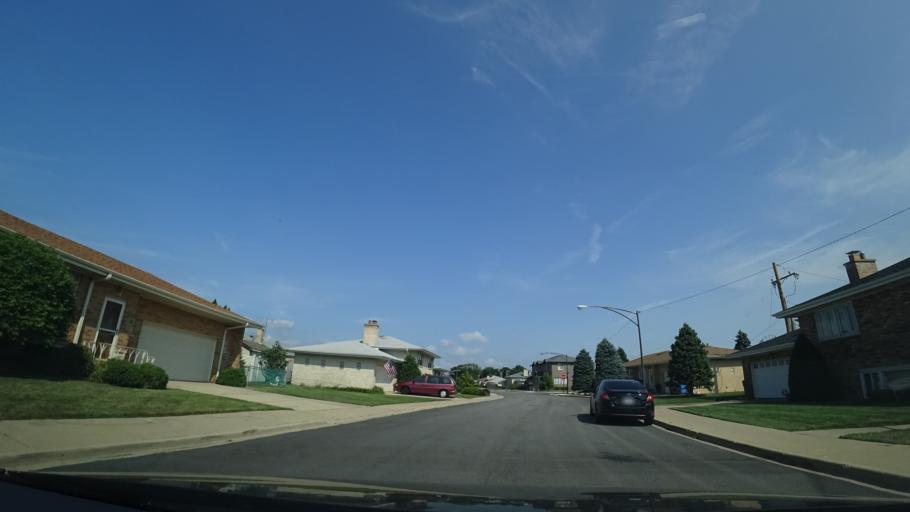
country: US
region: Illinois
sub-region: Cook County
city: Norridge
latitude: 41.9652
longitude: -87.8426
